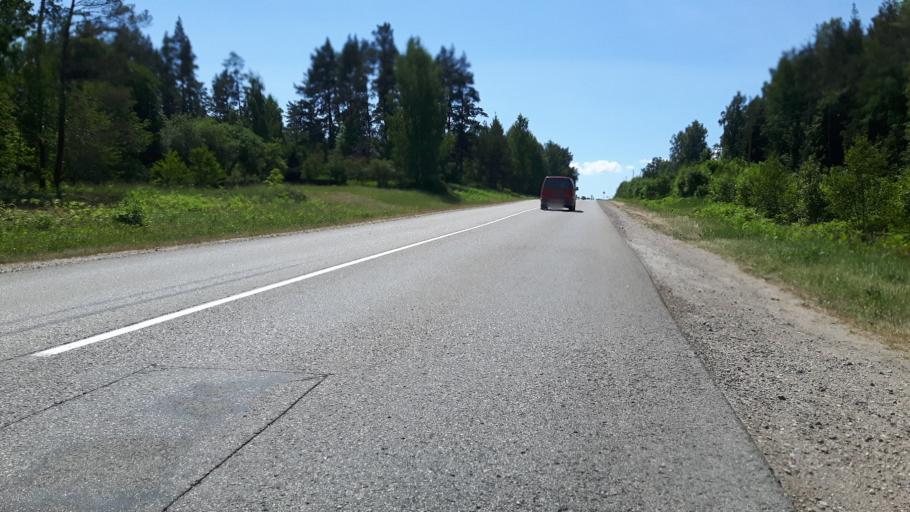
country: LV
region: Kuldigas Rajons
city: Kuldiga
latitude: 56.9429
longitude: 21.9330
